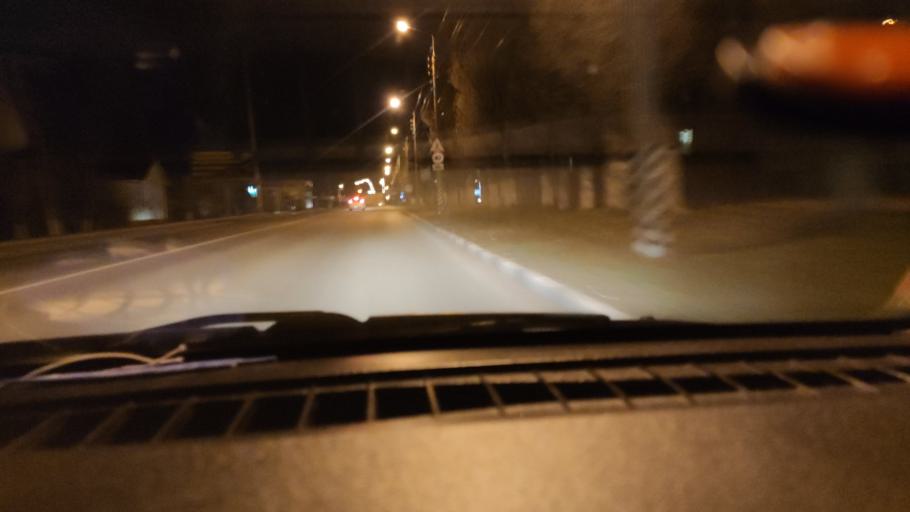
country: RU
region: Saratov
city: Privolzhskiy
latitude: 51.4106
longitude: 46.0416
